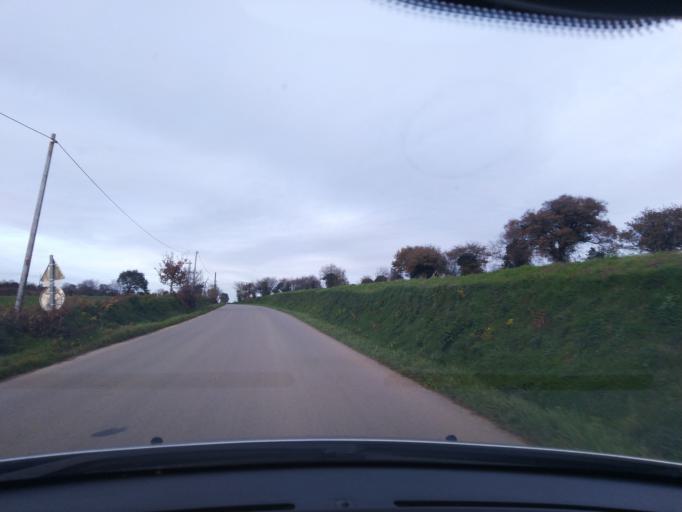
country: FR
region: Brittany
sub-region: Departement du Finistere
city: Guerlesquin
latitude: 48.5484
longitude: -3.6197
